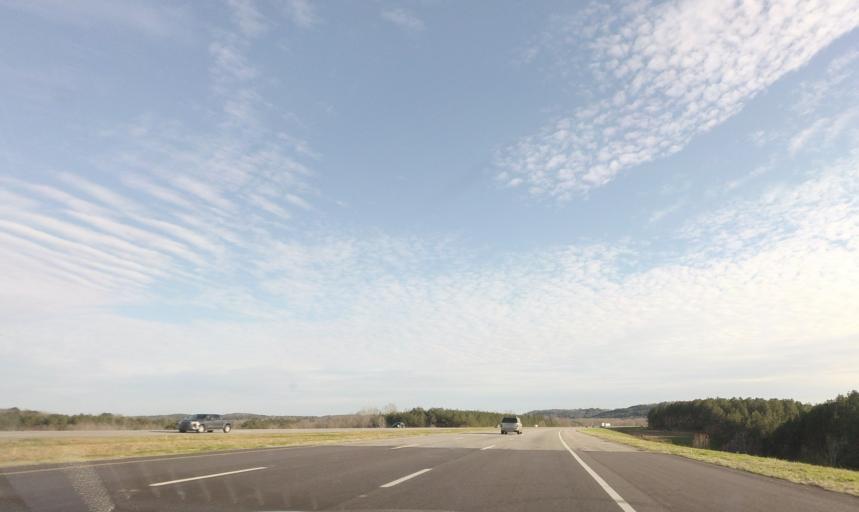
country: US
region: Alabama
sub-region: Walker County
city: Cordova
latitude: 33.7860
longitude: -87.2153
